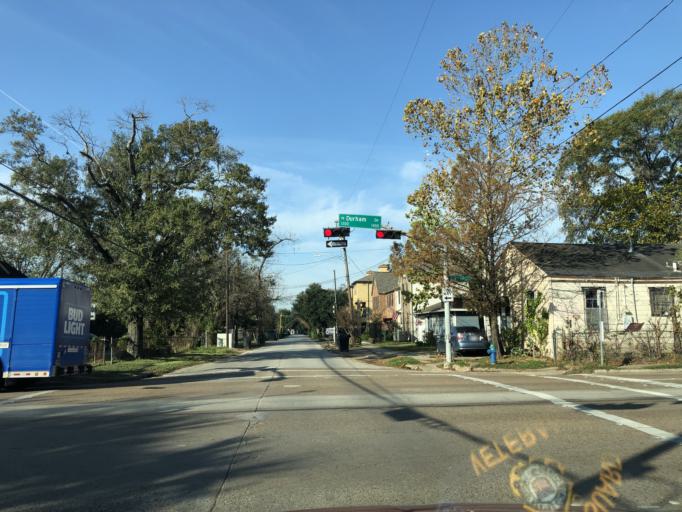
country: US
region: Texas
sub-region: Harris County
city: Houston
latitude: 29.7961
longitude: -95.4115
